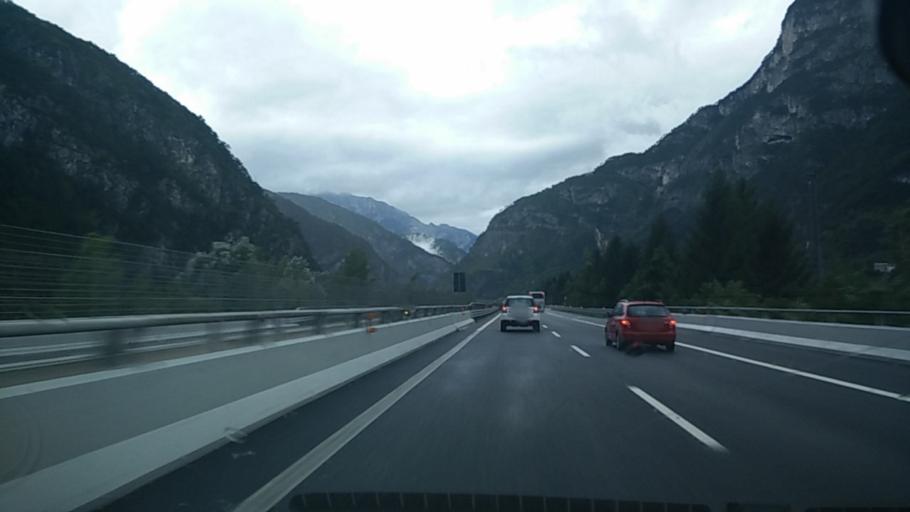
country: IT
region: Friuli Venezia Giulia
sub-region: Provincia di Udine
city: Chiusaforte
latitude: 46.4051
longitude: 13.3090
